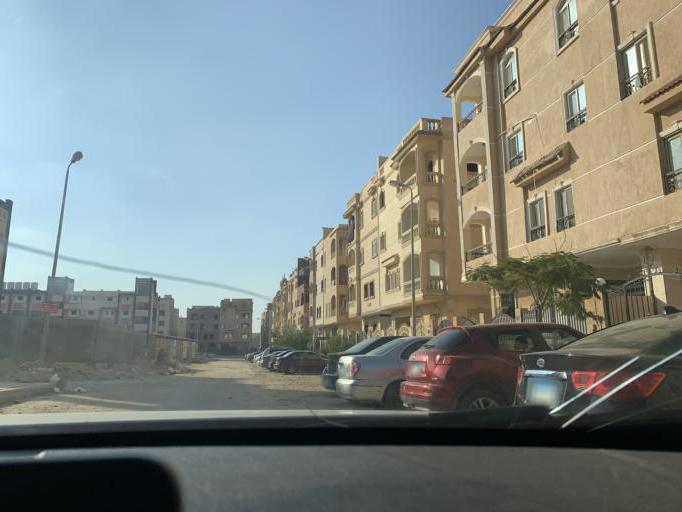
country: EG
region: Muhafazat al Qalyubiyah
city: Al Khankah
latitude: 30.0031
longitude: 31.4848
